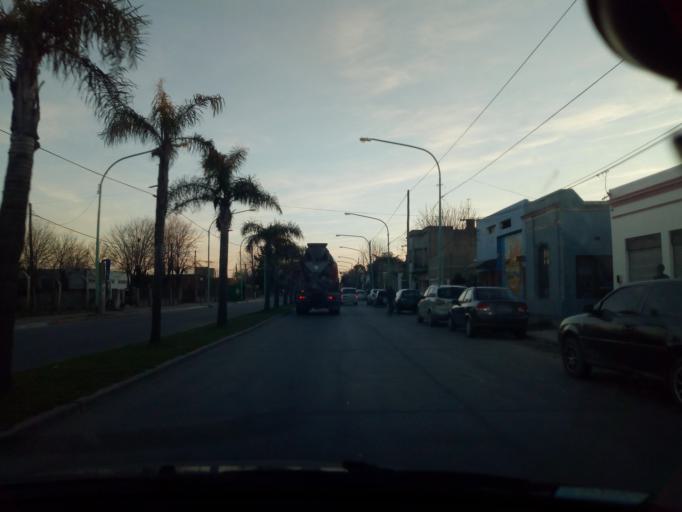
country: AR
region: Buenos Aires
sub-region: Partido de Ensenada
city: Ensenada
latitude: -34.8691
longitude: -57.9098
